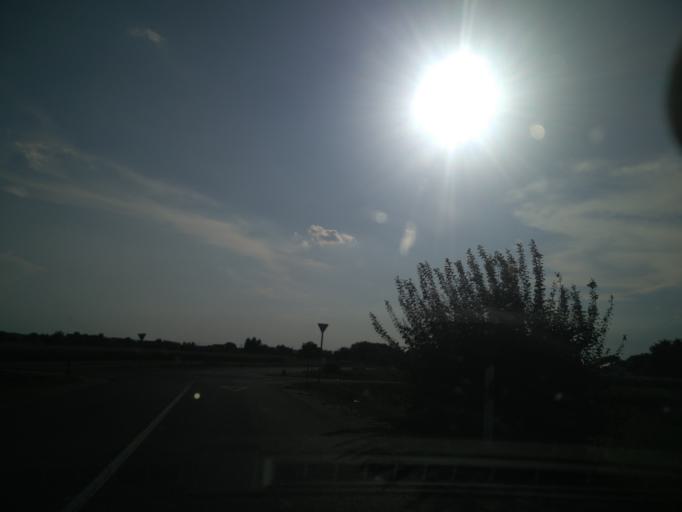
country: HU
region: Zala
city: Zalaegerszeg
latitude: 46.8794
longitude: 16.8304
